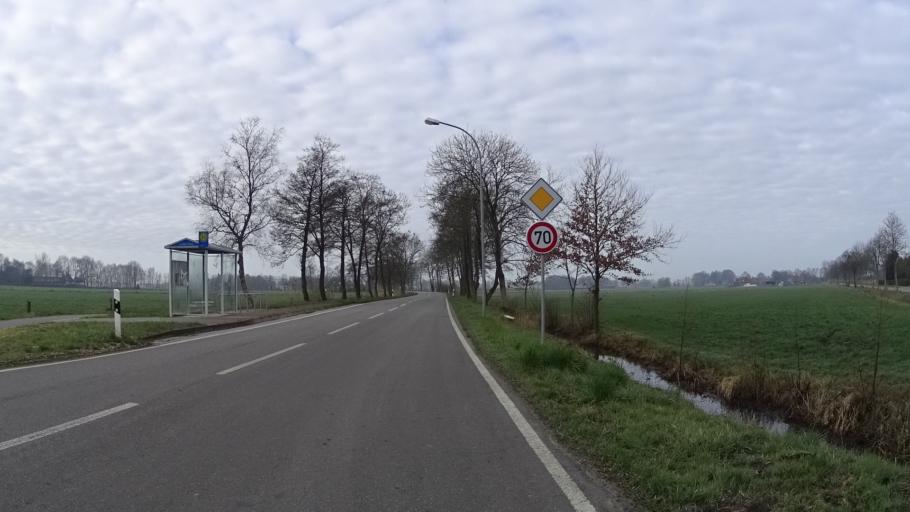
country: DE
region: Lower Saxony
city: Upgant-Schott
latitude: 53.4401
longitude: 7.3237
